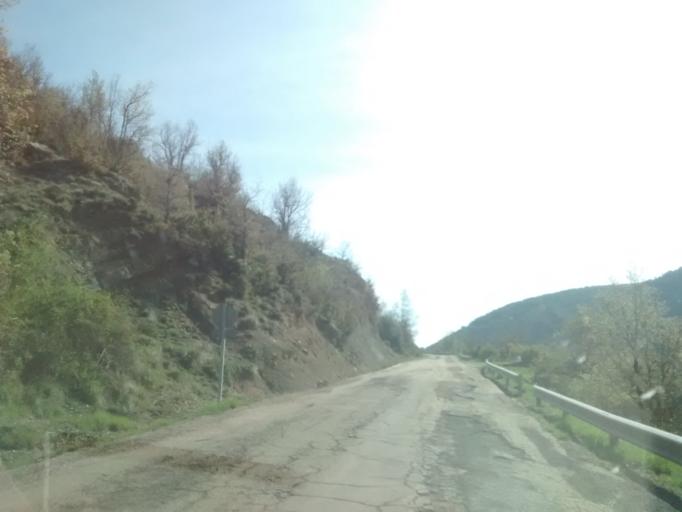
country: ES
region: Aragon
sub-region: Provincia de Huesca
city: Arguis
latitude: 42.3214
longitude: -0.4349
